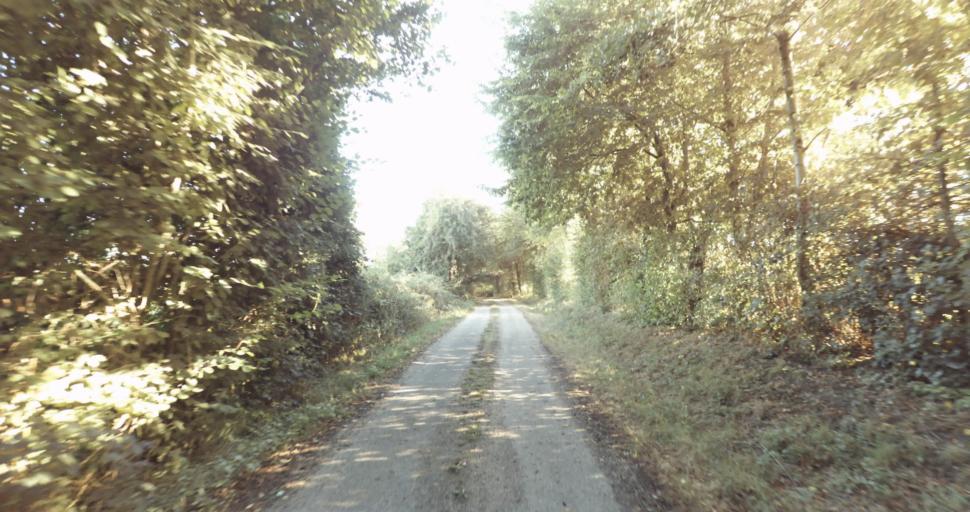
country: FR
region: Lower Normandy
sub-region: Departement de l'Orne
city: Vimoutiers
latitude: 48.8995
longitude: 0.1458
